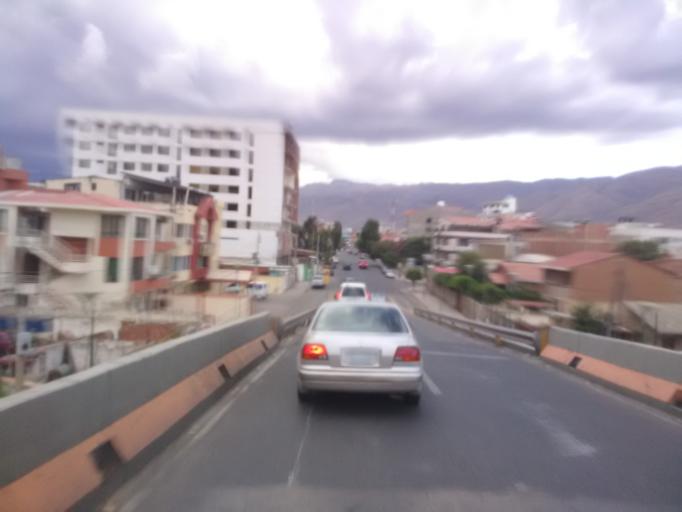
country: BO
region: Cochabamba
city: Cochabamba
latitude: -17.3869
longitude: -66.1661
